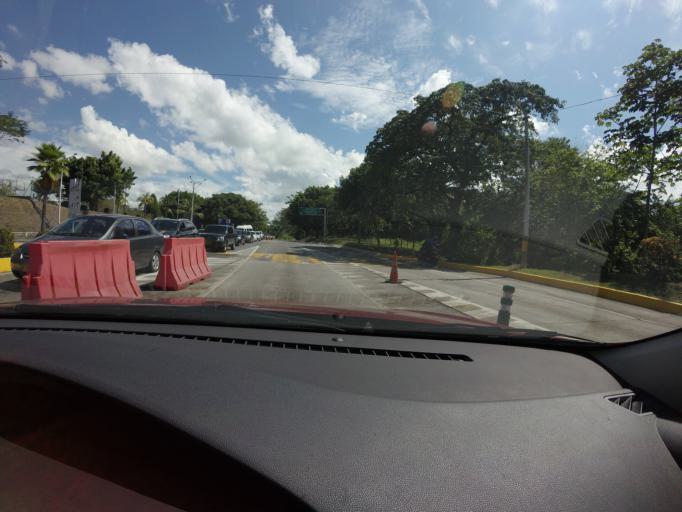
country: CO
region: Antioquia
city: Puerto Triunfo
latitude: 5.8725
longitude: -74.6113
